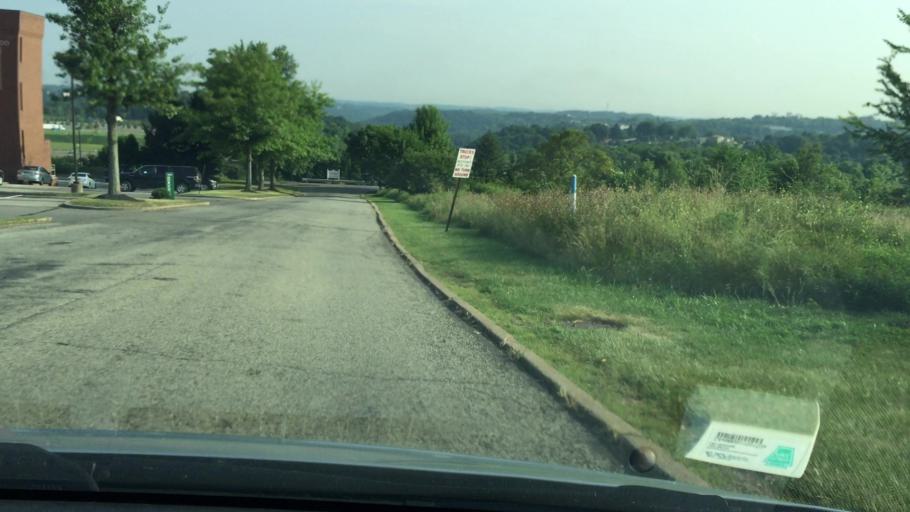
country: US
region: Pennsylvania
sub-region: Allegheny County
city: Rennerdale
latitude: 40.4489
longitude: -80.1538
